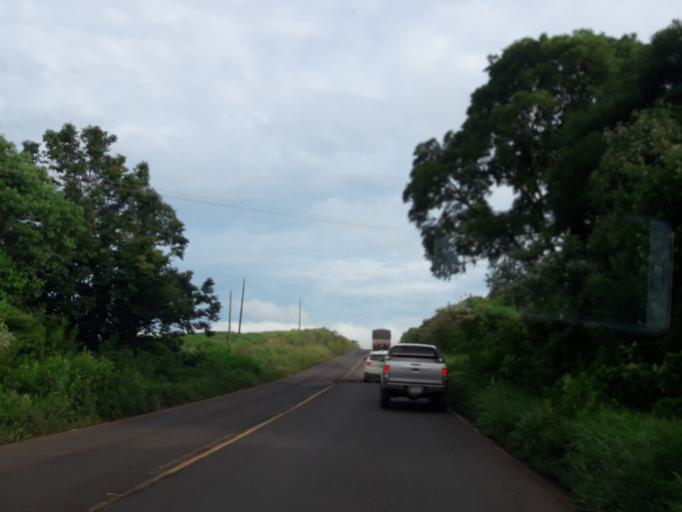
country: AR
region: Misiones
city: Bernardo de Irigoyen
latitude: -26.3526
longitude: -53.5441
